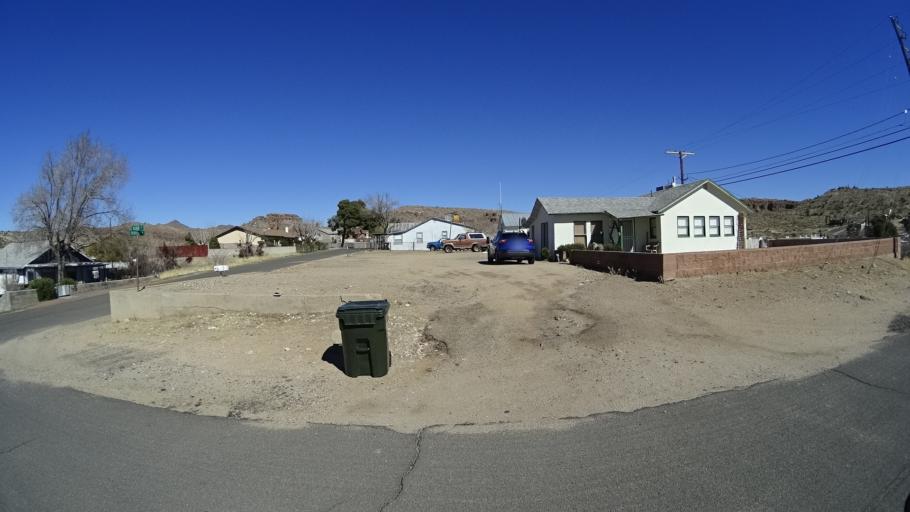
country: US
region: Arizona
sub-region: Mohave County
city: Kingman
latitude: 35.1954
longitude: -114.0617
